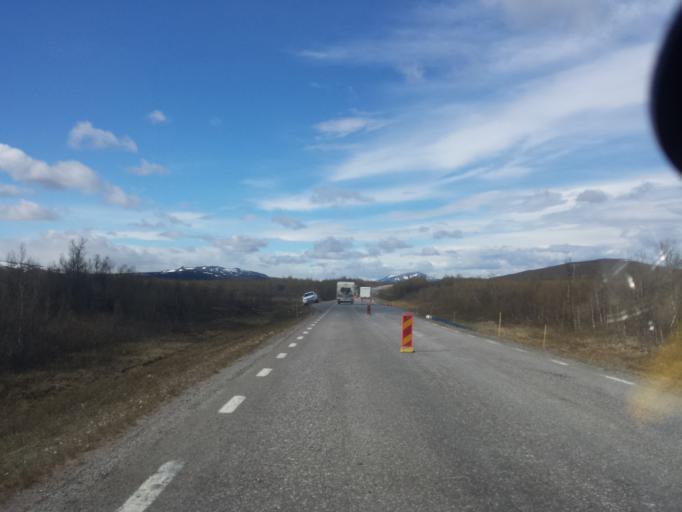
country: SE
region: Norrbotten
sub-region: Kiruna Kommun
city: Kiruna
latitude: 68.0129
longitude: 19.8421
